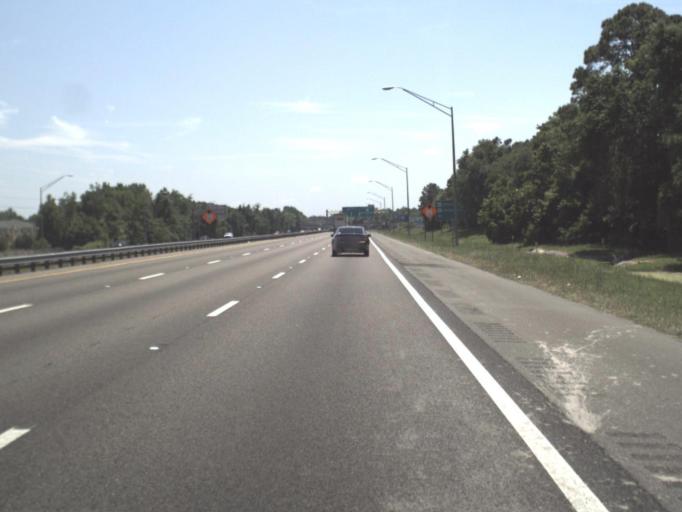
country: US
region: Florida
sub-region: Clay County
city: Bellair-Meadowbrook Terrace
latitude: 30.2340
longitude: -81.7631
